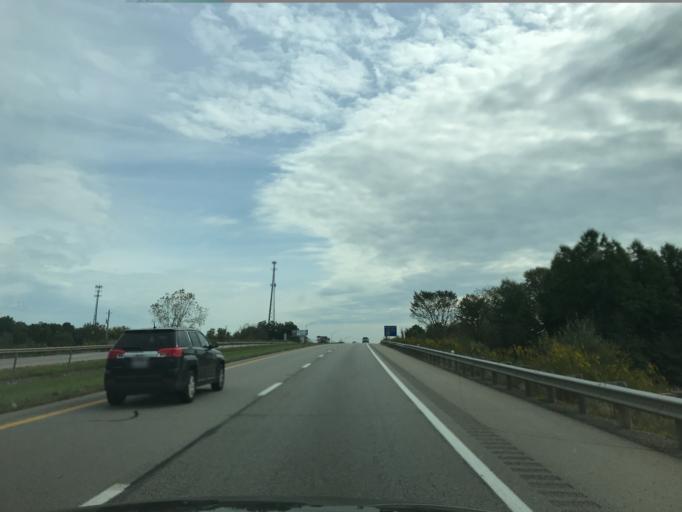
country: US
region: Ohio
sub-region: Trumbull County
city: Champion Heights
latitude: 41.2762
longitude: -80.8527
